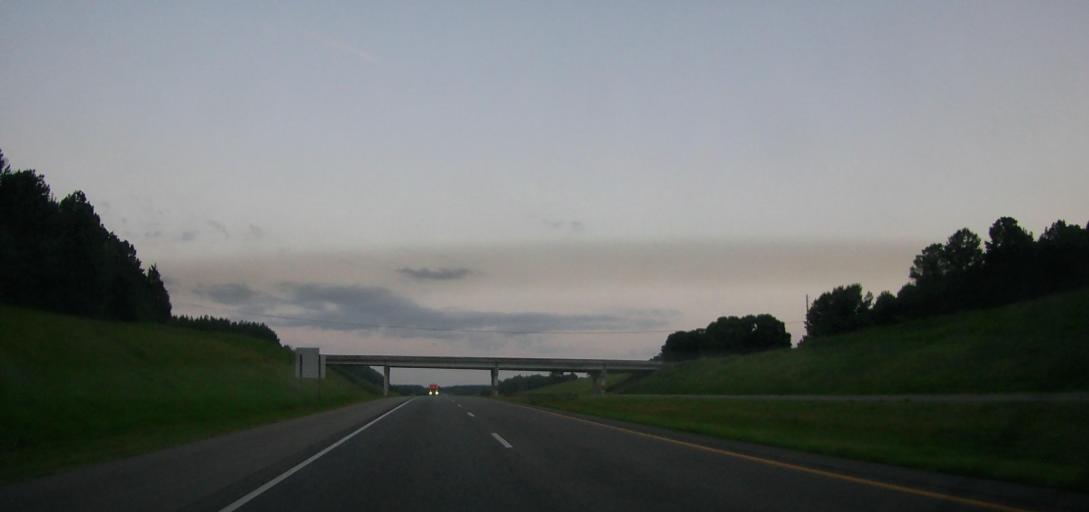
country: US
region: Alabama
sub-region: Marion County
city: Hamilton
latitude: 34.1487
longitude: -88.0591
